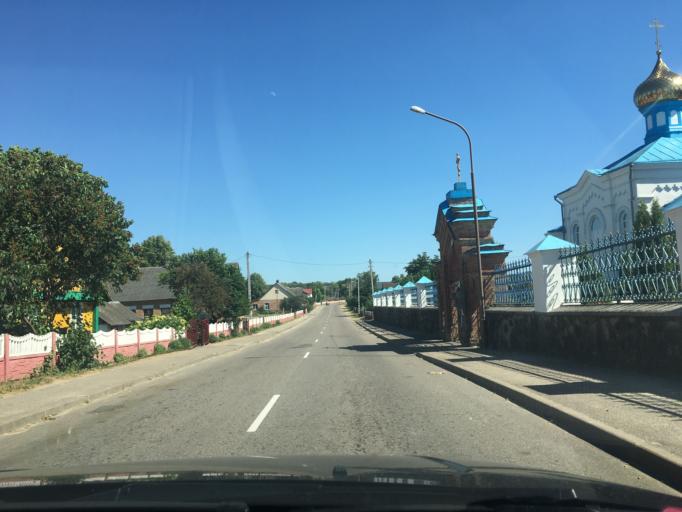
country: BY
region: Grodnenskaya
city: Hal'shany
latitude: 54.2561
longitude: 26.0131
